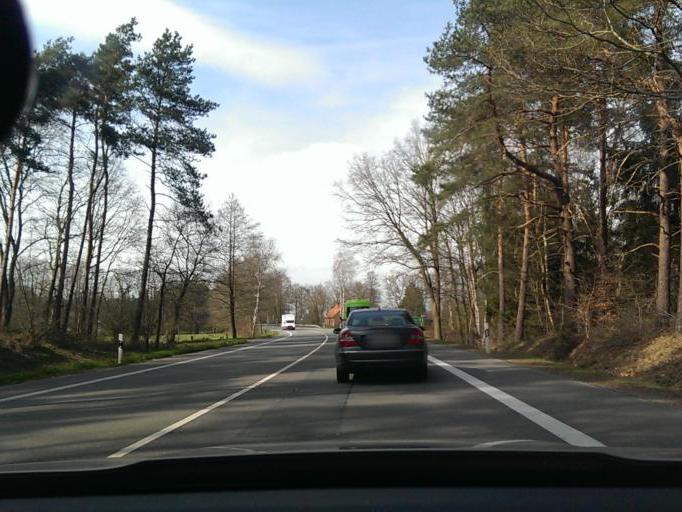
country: DE
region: North Rhine-Westphalia
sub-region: Regierungsbezirk Detmold
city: Hovelhof
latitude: 51.8462
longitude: 8.6659
